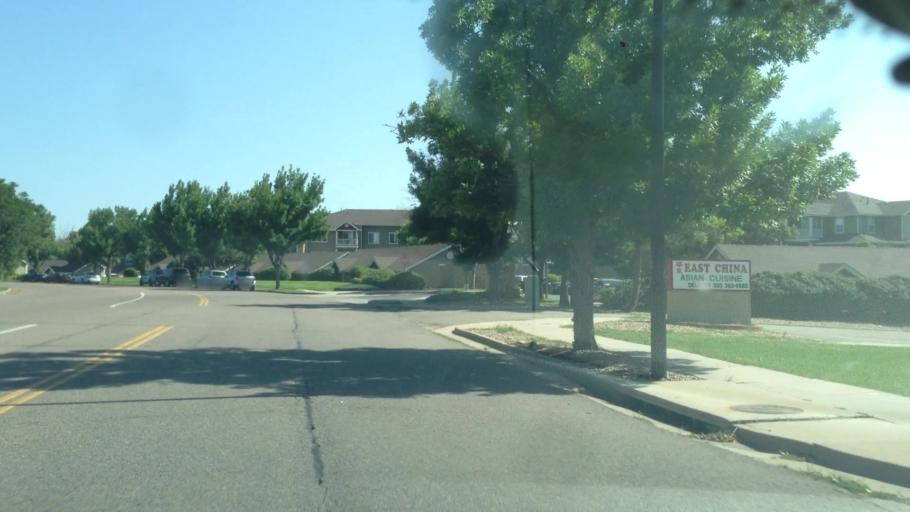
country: US
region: Colorado
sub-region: Adams County
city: Aurora
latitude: 39.7246
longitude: -104.8082
